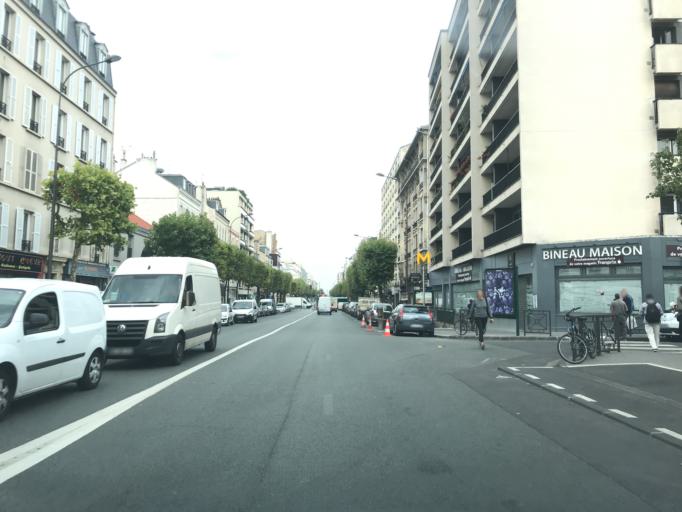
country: FR
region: Ile-de-France
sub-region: Departement du Val-de-Marne
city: Vincennes
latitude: 48.8453
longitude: 2.4309
